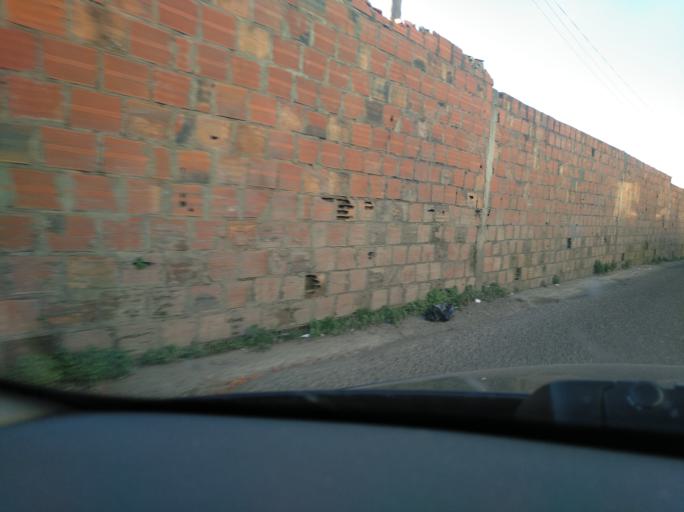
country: PT
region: Lisbon
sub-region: Odivelas
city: Pontinha
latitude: 38.7717
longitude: -9.1810
